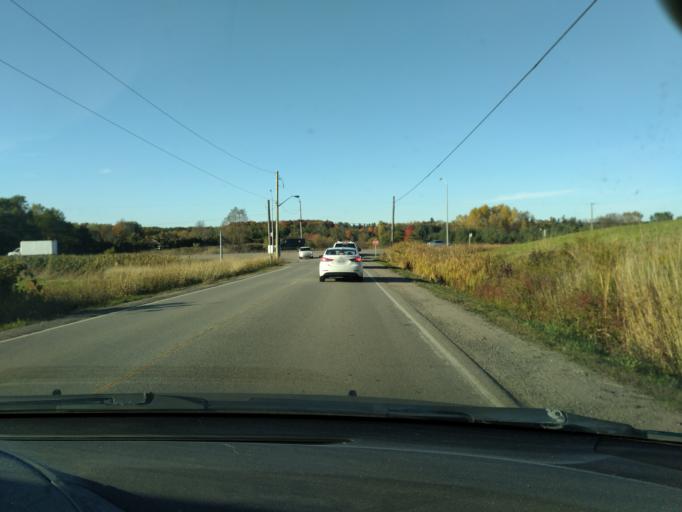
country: CA
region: Ontario
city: Bradford West Gwillimbury
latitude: 43.9993
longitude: -79.7275
